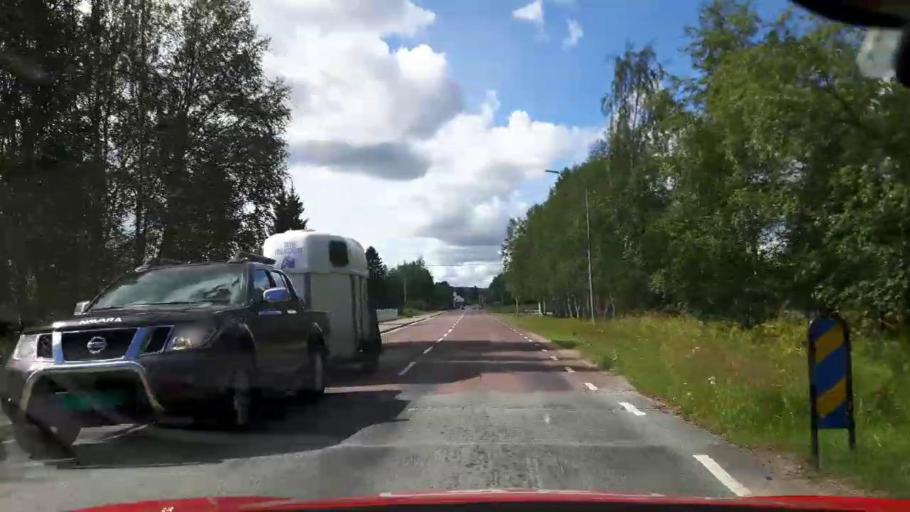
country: SE
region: Jaemtland
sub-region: Harjedalens Kommun
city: Sveg
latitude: 61.8539
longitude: 14.0840
